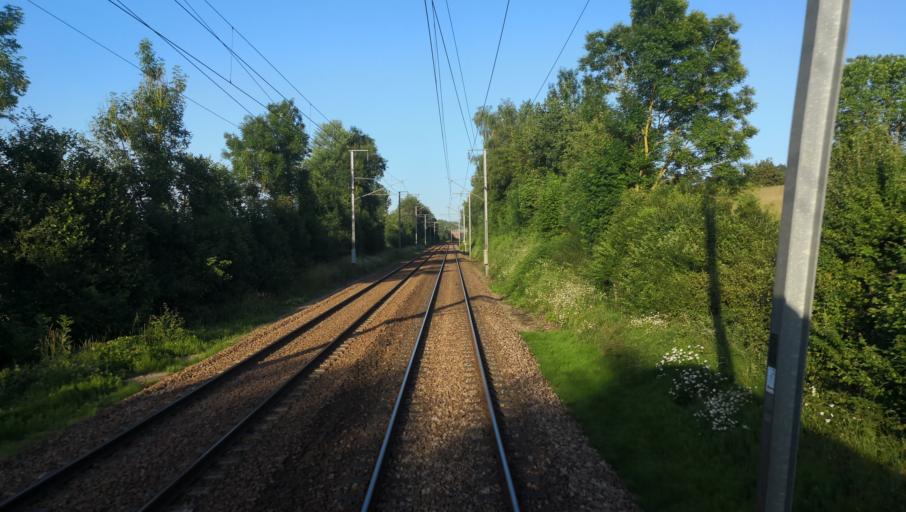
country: FR
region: Lower Normandy
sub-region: Departement du Calvados
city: Beuvillers
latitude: 49.1224
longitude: 0.3203
